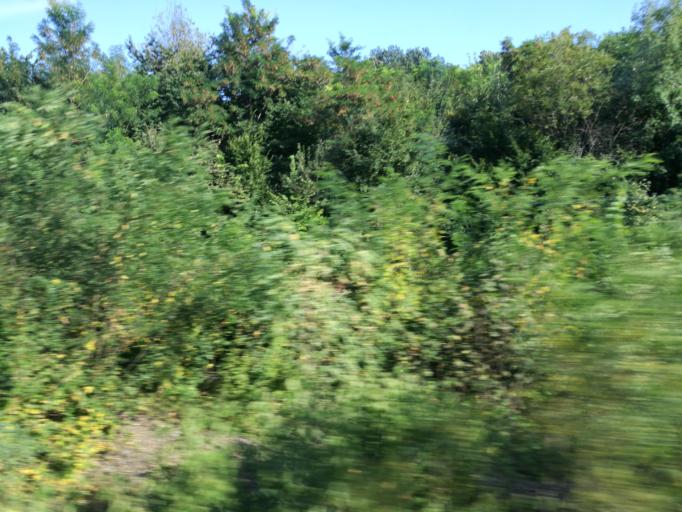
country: RO
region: Iasi
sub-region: Comuna Ciurea
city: Ciurea
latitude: 47.0170
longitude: 27.5761
